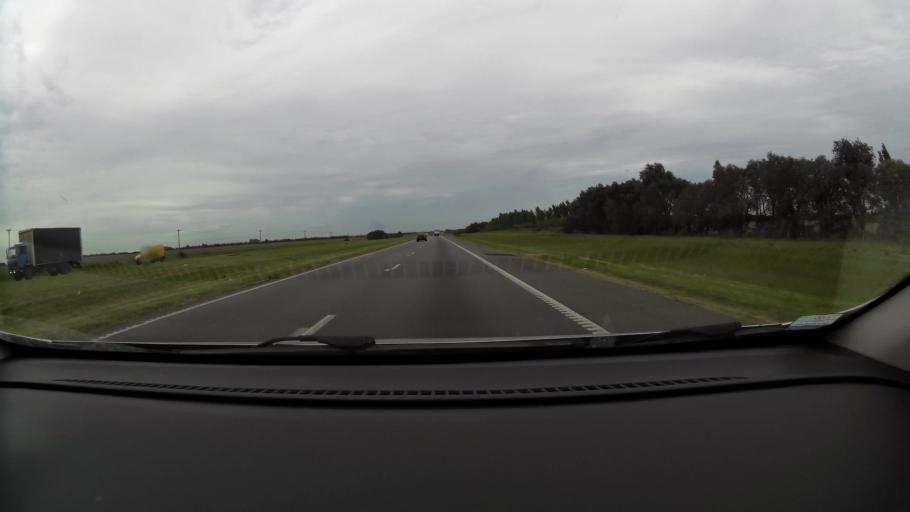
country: AR
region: Buenos Aires
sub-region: Partido de Baradero
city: Baradero
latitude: -33.9878
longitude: -59.3712
